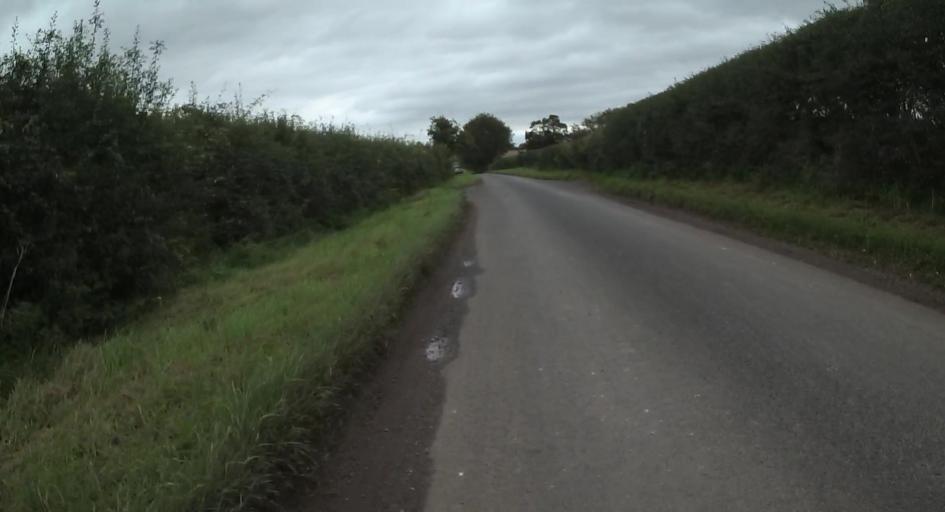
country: GB
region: England
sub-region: Hampshire
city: Four Marks
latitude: 51.1610
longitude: -1.1232
